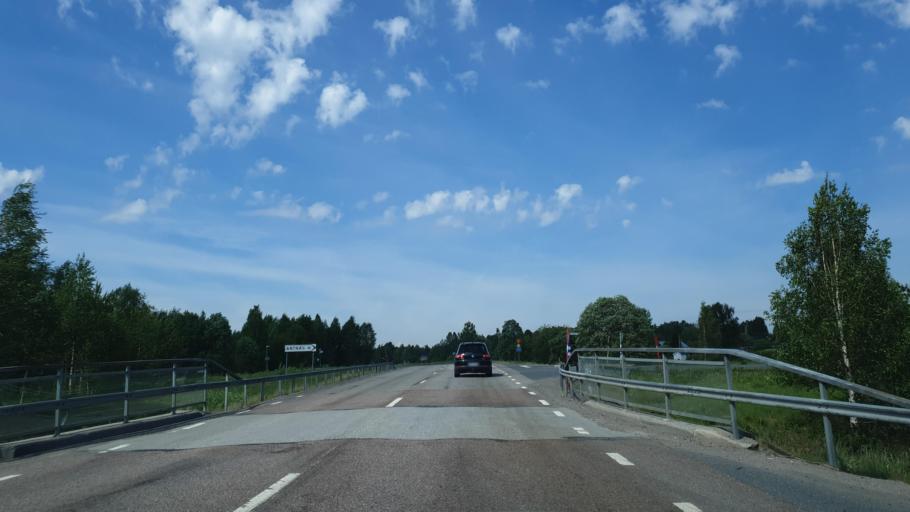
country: SE
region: Norrbotten
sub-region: Lulea Kommun
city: Sodra Sunderbyn
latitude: 65.5509
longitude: 21.8441
